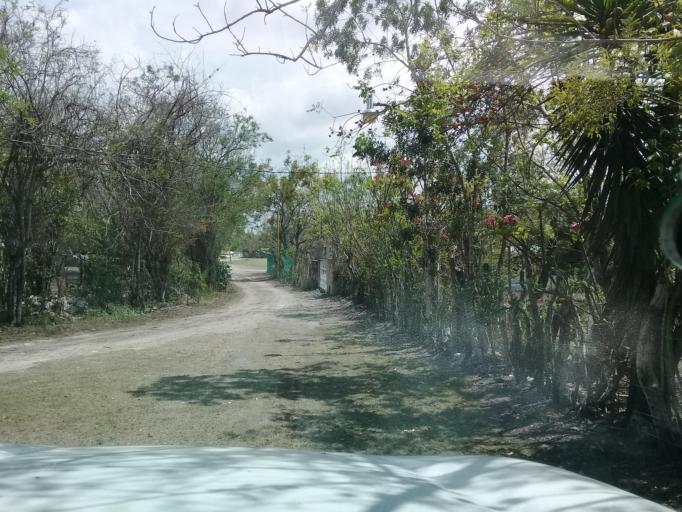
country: MX
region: Veracruz
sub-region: Emiliano Zapata
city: Plan del Rio
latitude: 19.3503
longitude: -96.6457
